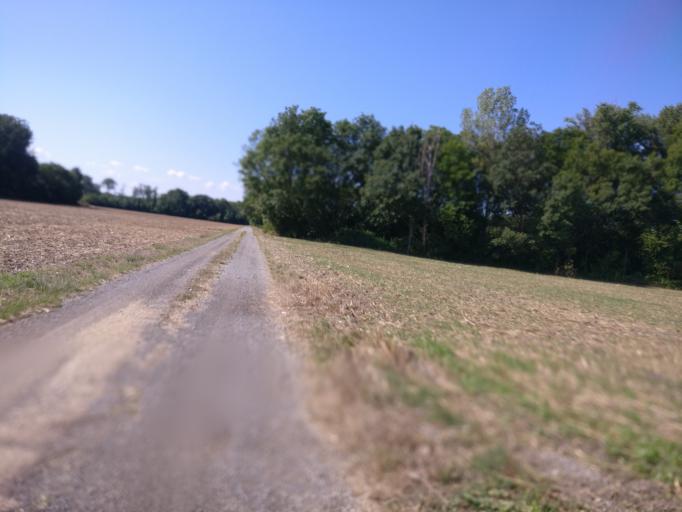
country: AT
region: Lower Austria
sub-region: Politischer Bezirk Baden
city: Pottendorf
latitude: 47.9295
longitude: 16.3695
